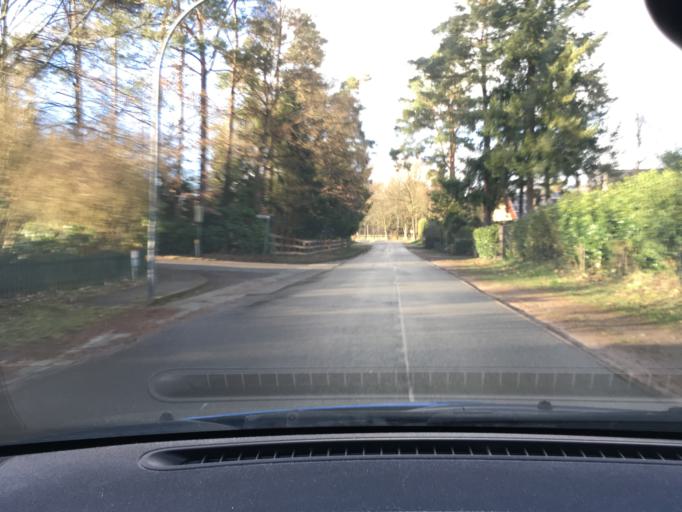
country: DE
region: Lower Saxony
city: Jesteburg
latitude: 53.3052
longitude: 9.9864
